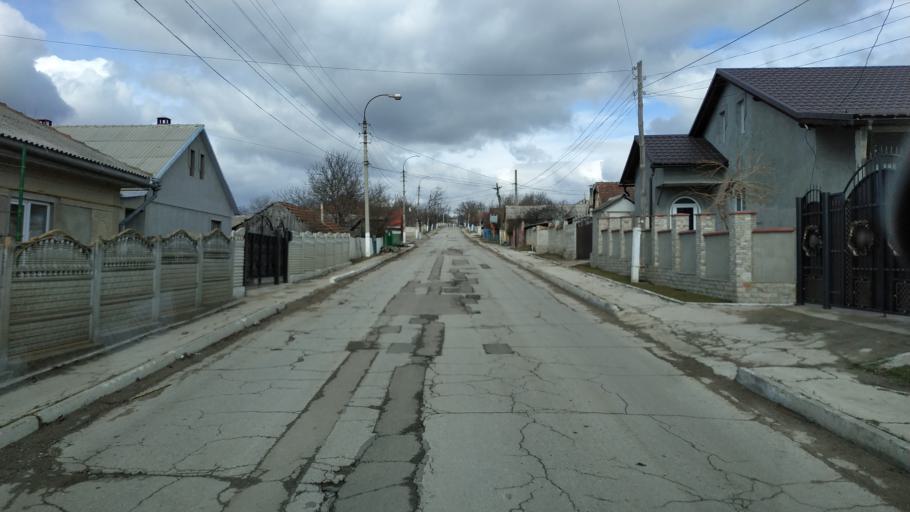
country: MD
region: Stinga Nistrului
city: Bucovat
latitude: 47.2065
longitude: 28.4967
